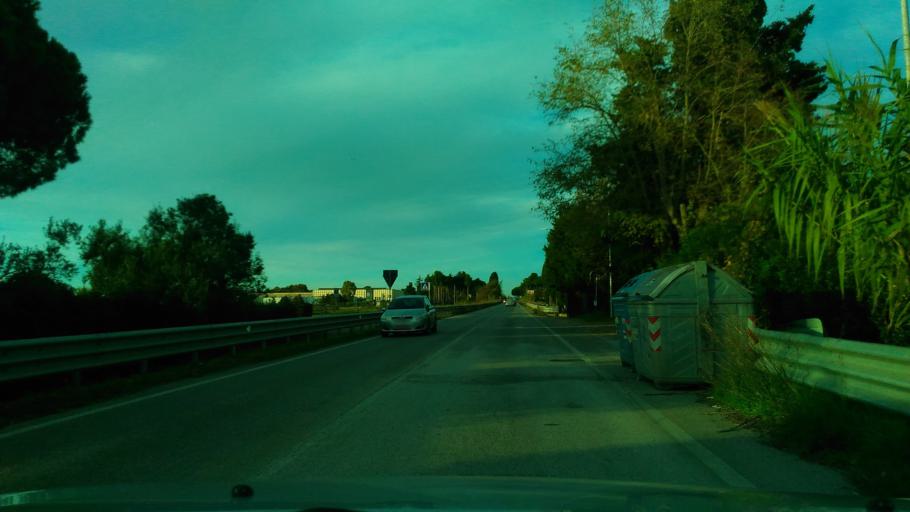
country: IT
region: Tuscany
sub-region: Provincia di Livorno
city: S.P. in Palazzi
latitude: 43.3415
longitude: 10.5049
